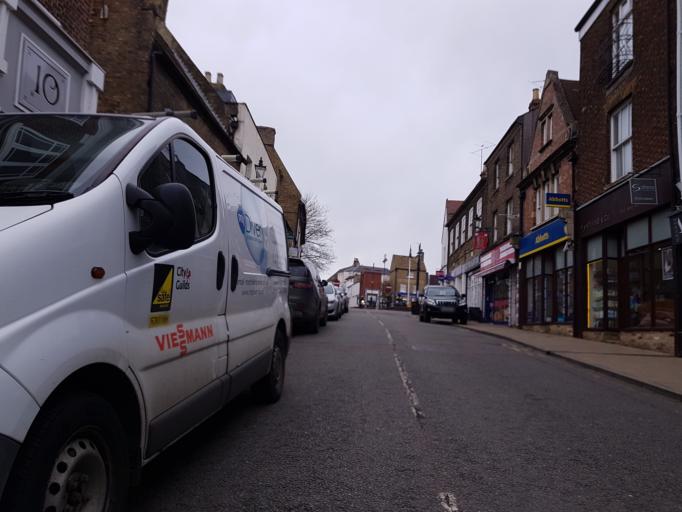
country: GB
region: England
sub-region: Cambridgeshire
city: Ely
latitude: 52.3987
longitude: 0.2671
